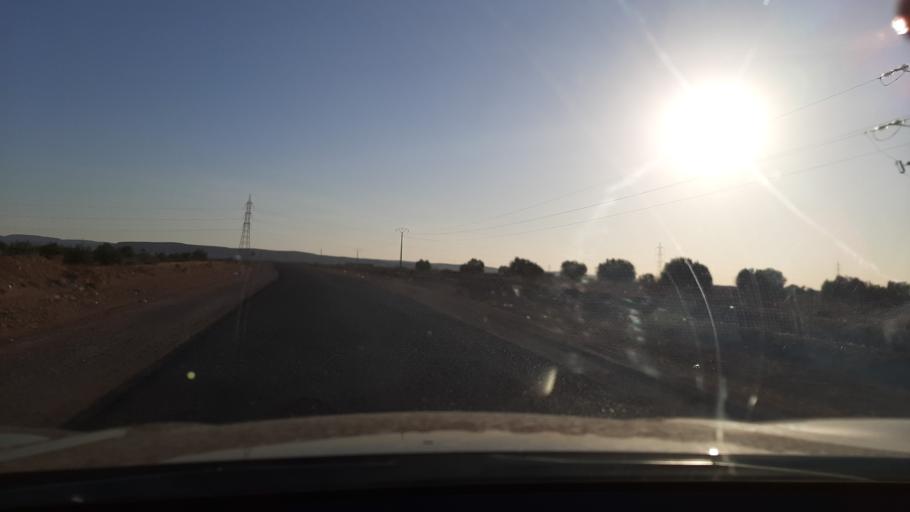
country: TN
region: Qabis
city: Matmata
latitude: 33.6168
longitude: 10.2356
